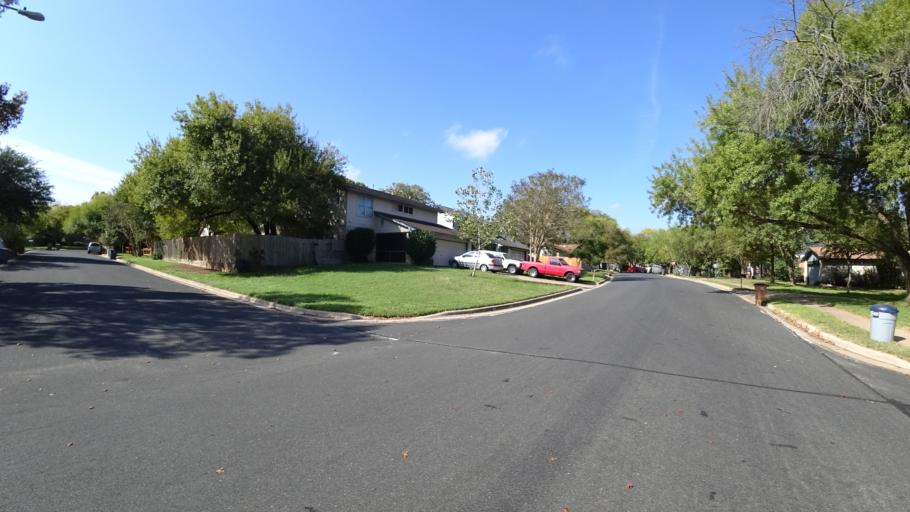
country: US
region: Texas
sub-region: Travis County
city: Shady Hollow
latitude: 30.1929
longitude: -97.8221
